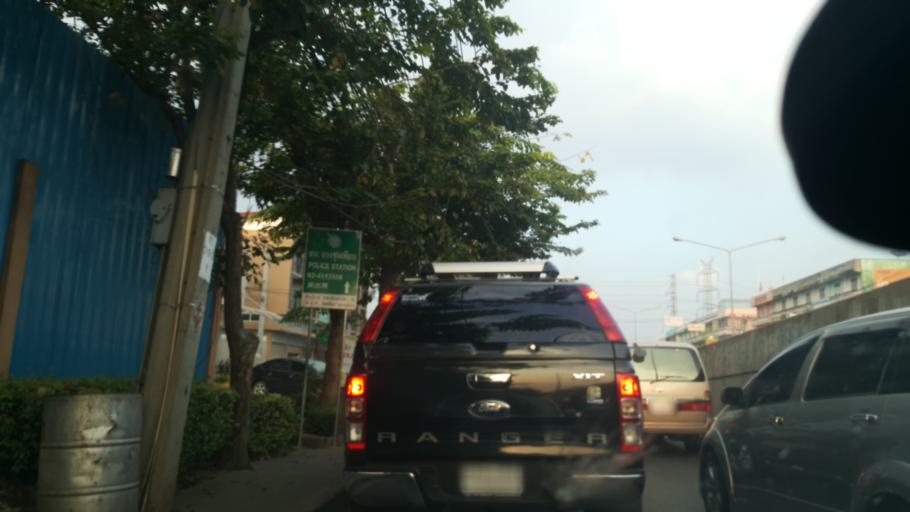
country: TH
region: Bangkok
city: Bang Bon
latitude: 13.6639
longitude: 100.4072
